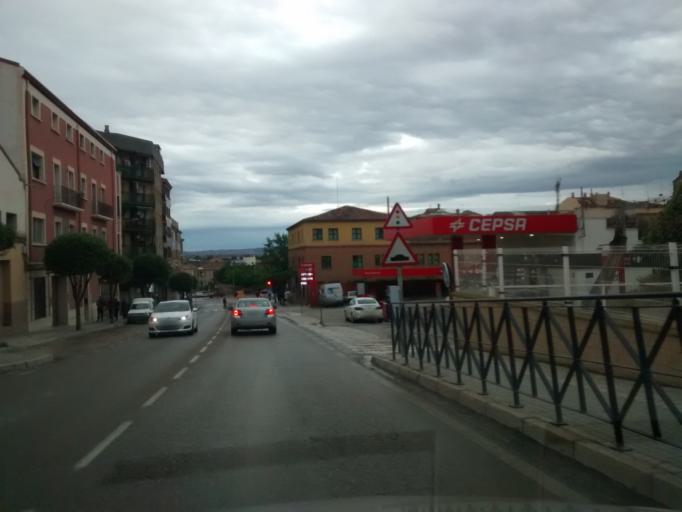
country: ES
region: Aragon
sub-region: Provincia de Zaragoza
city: Caspe
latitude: 41.2353
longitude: -0.0443
